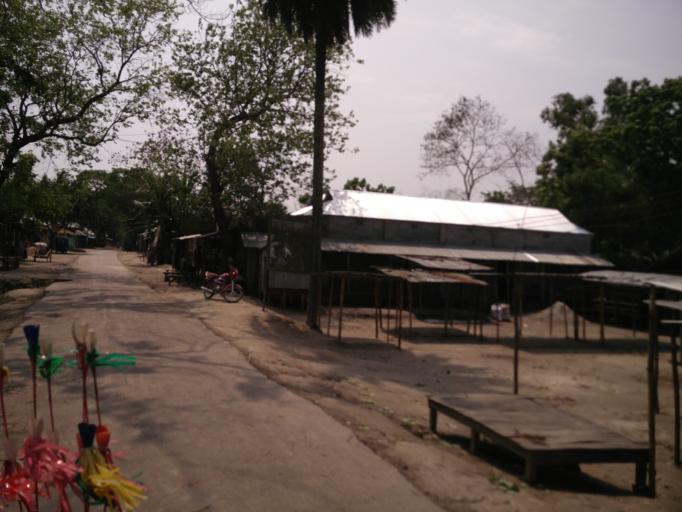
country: BD
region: Dhaka
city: Sherpur
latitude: 24.9458
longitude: 90.1604
